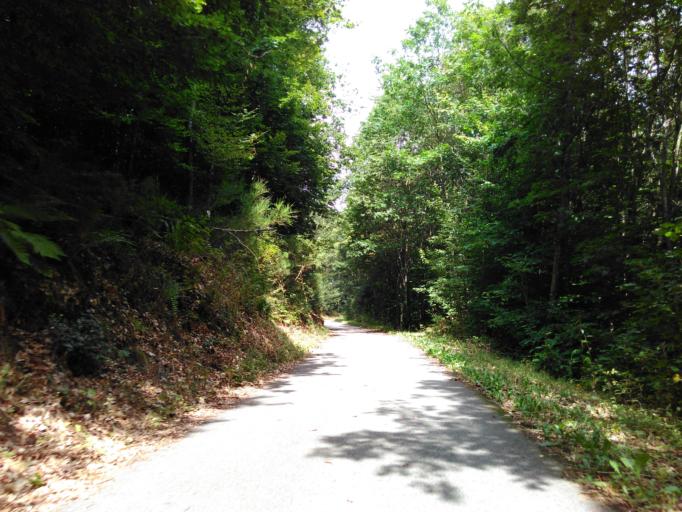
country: LU
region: Grevenmacher
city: Gonderange
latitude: 49.6657
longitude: 6.2268
